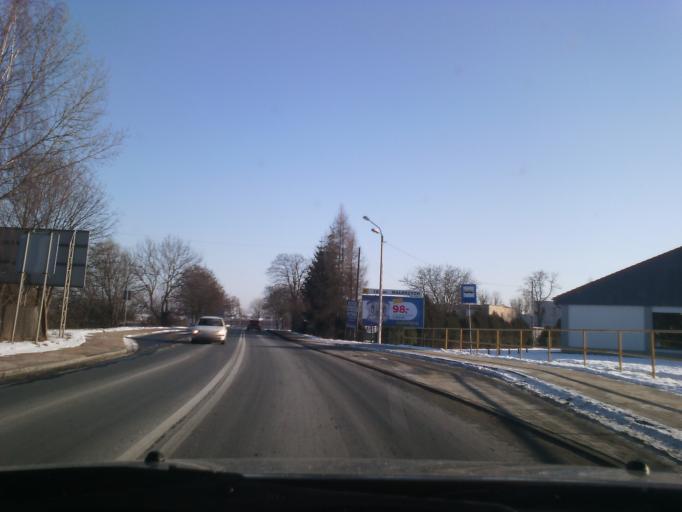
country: PL
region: Lower Silesian Voivodeship
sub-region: Powiat swidnicki
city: Strzegom
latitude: 50.9535
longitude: 16.3525
